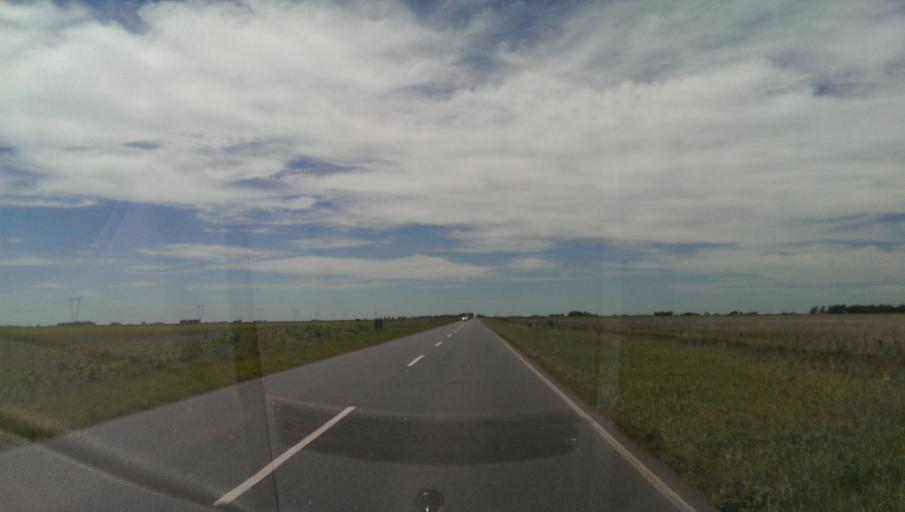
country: AR
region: Buenos Aires
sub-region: Partido de Laprida
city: Laprida
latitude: -37.2287
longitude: -60.7061
